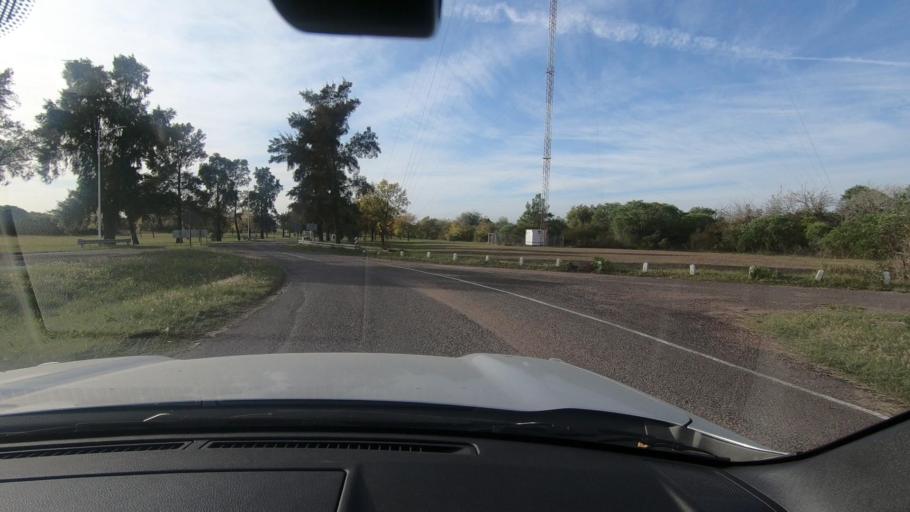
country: AR
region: Entre Rios
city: Colon
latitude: -32.2446
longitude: -58.1871
